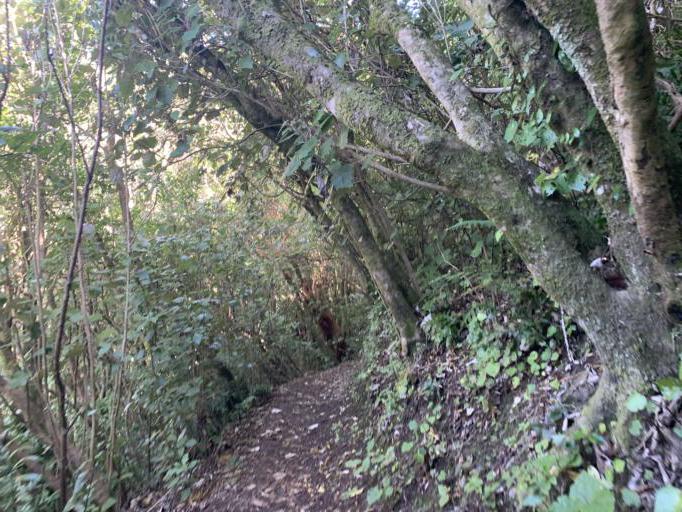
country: NZ
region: Wellington
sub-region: Wellington City
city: Brooklyn
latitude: -41.3003
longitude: 174.7533
